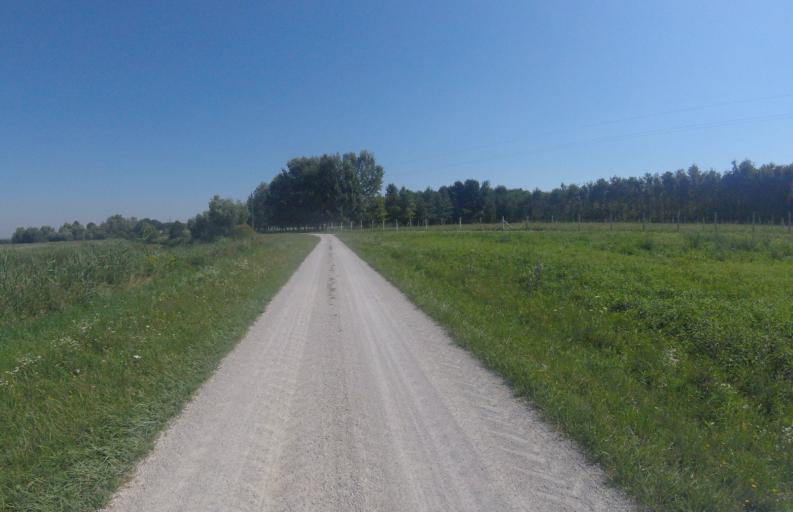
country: HU
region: Zala
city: Keszthely
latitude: 46.6988
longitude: 17.2374
